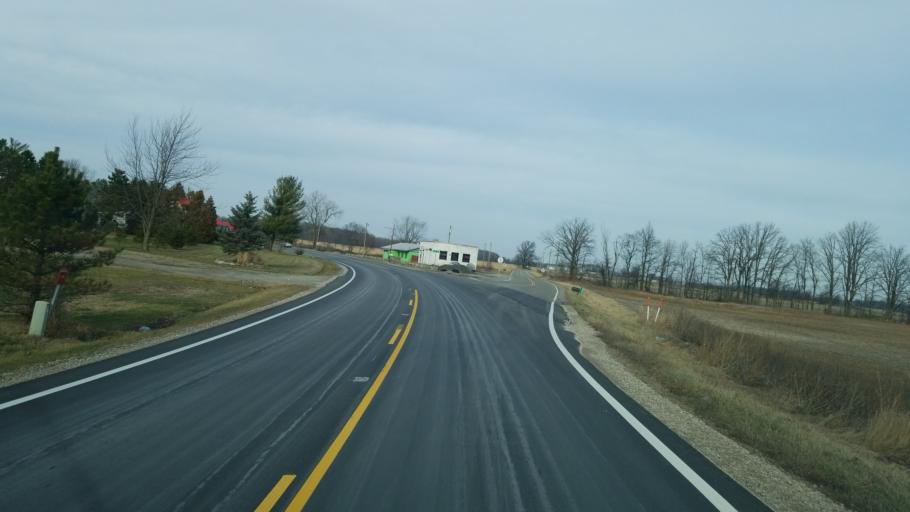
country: US
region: Ohio
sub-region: Union County
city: Richwood
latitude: 40.4048
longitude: -83.4114
